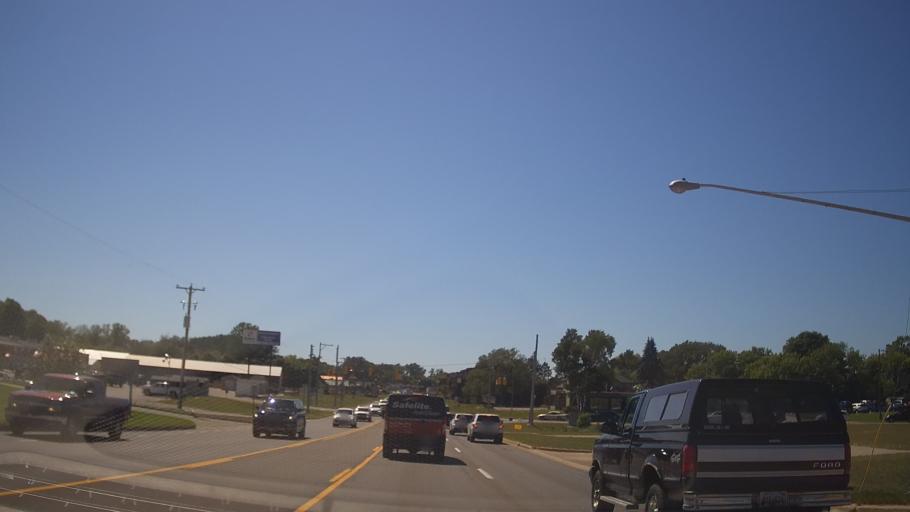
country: US
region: Michigan
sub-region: Emmet County
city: Petoskey
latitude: 45.3892
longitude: -84.9109
